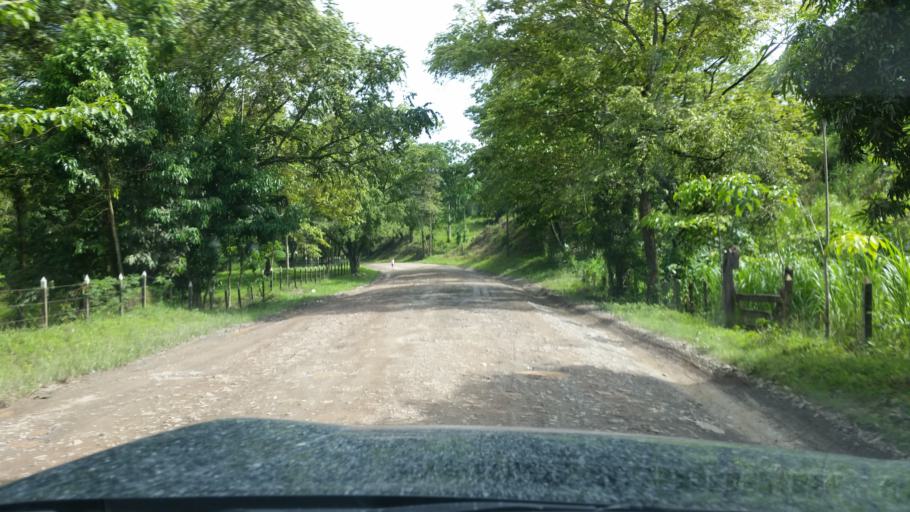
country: NI
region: Atlantico Norte (RAAN)
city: Siuna
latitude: 13.6308
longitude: -84.7953
